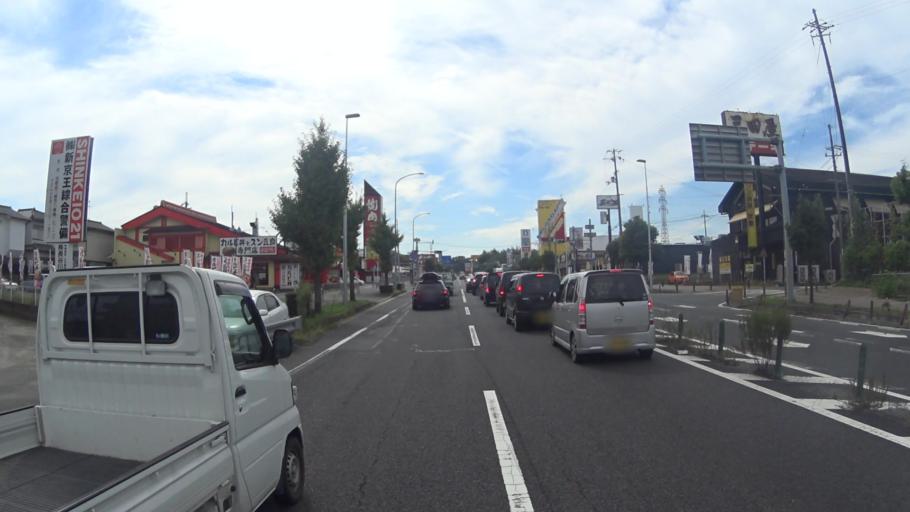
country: JP
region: Kyoto
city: Yawata
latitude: 34.8568
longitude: 135.7105
